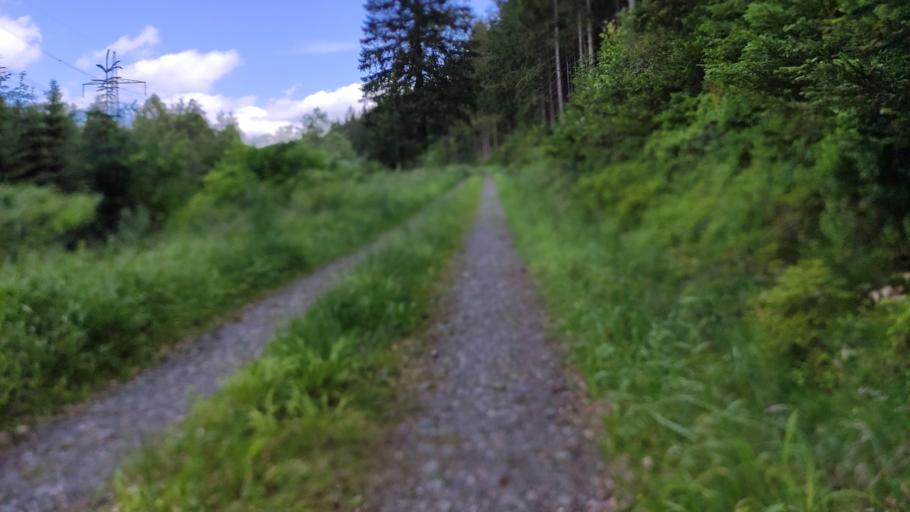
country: DE
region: Bavaria
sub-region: Upper Franconia
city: Tschirn
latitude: 50.4116
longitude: 11.4674
